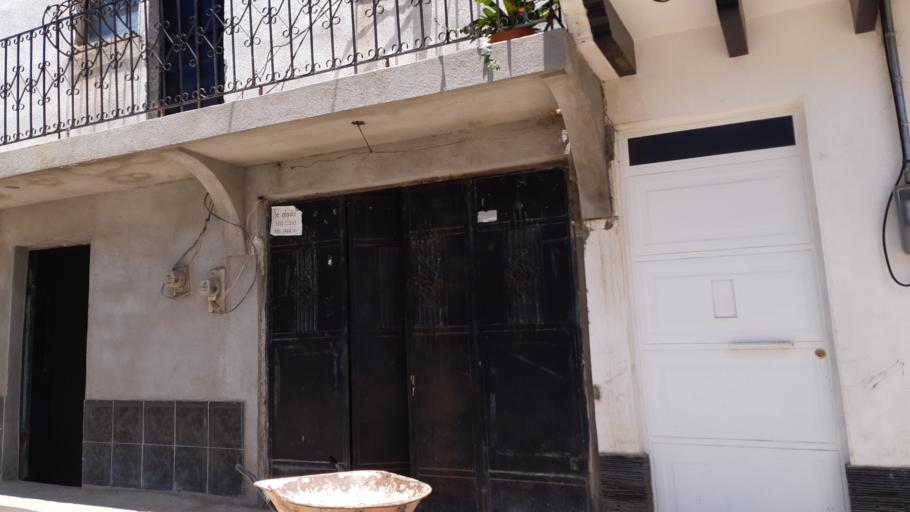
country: GT
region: Chimaltenango
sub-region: Municipio de Chimaltenango
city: Chimaltenango
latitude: 14.6636
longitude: -90.8446
